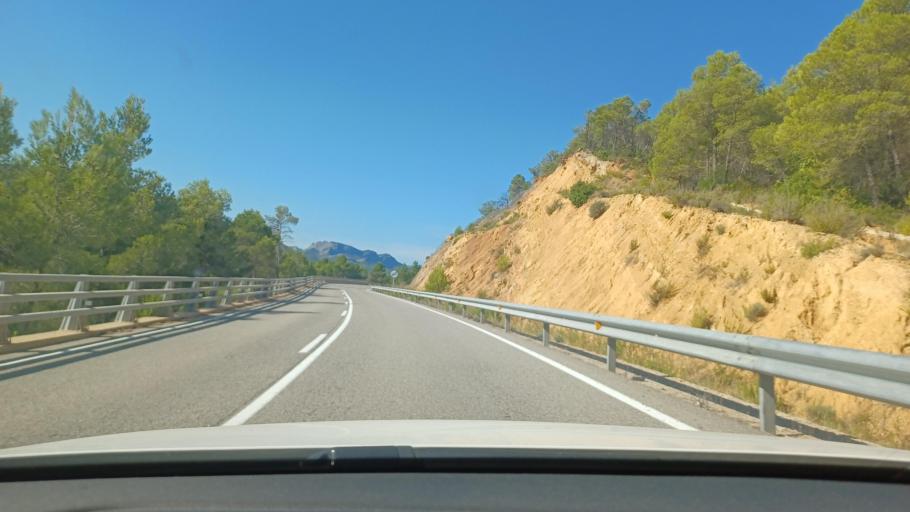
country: ES
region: Catalonia
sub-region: Provincia de Tarragona
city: Horta de Sant Joan
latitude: 40.9560
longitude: 0.3488
